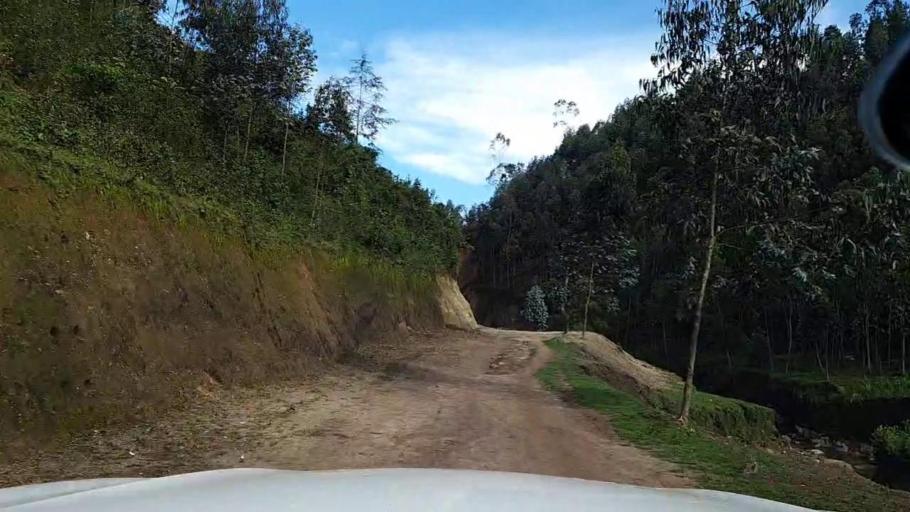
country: BI
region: Kayanza
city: Kayanza
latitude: -2.7809
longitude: 29.4522
